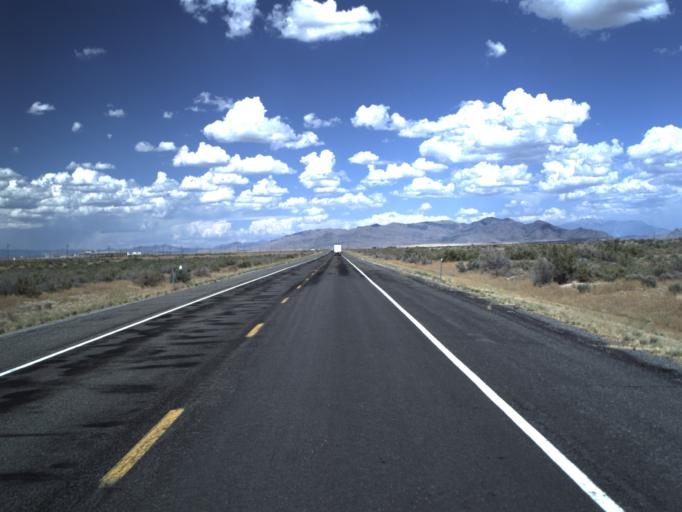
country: US
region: Utah
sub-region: Millard County
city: Delta
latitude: 39.4463
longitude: -112.4497
